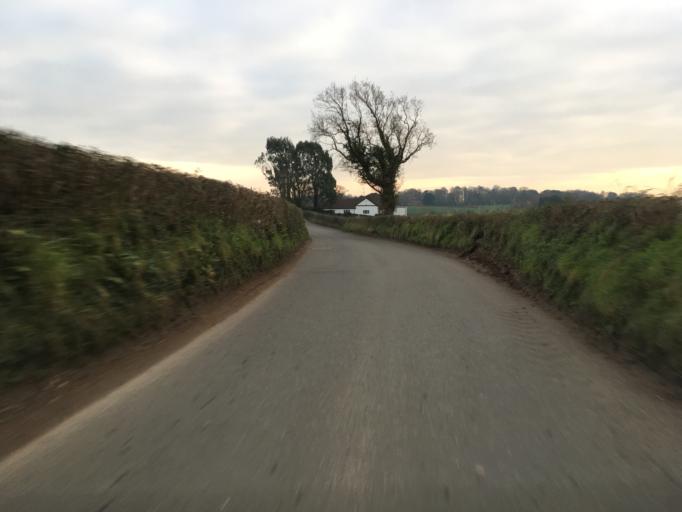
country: GB
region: Wales
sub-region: Newport
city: Marshfield
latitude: 51.5532
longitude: -3.0953
